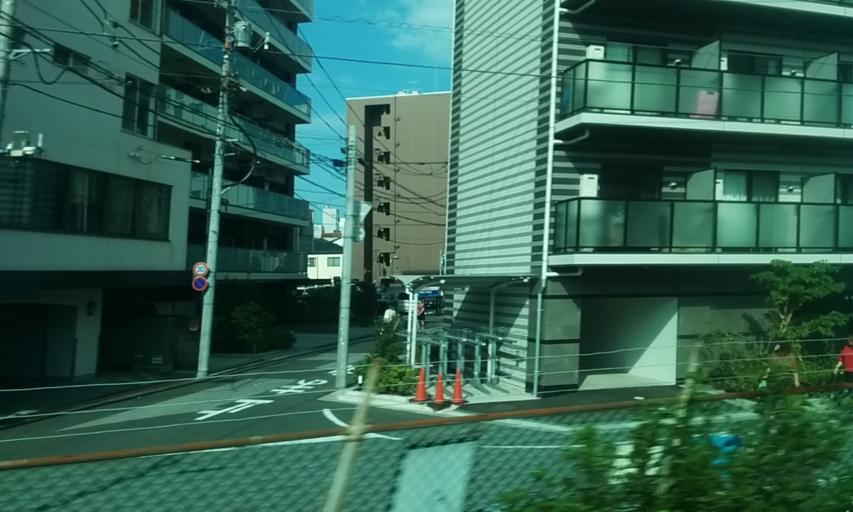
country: JP
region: Saitama
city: Kawaguchi
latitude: 35.8136
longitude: 139.7061
